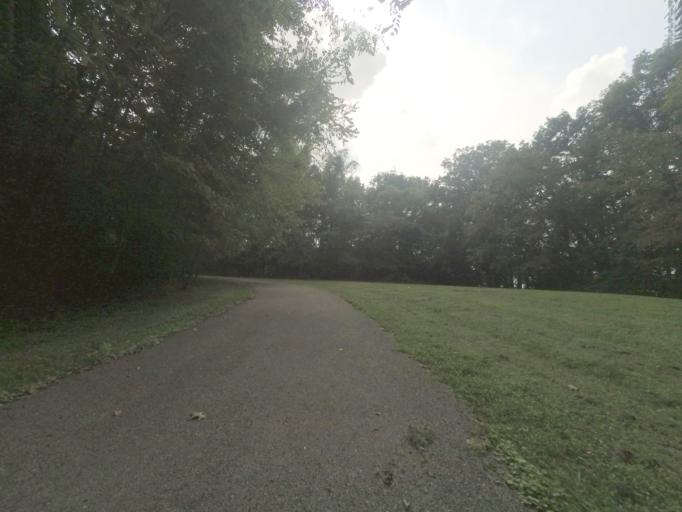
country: US
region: West Virginia
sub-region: Cabell County
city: Huntington
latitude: 38.4217
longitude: -82.3975
